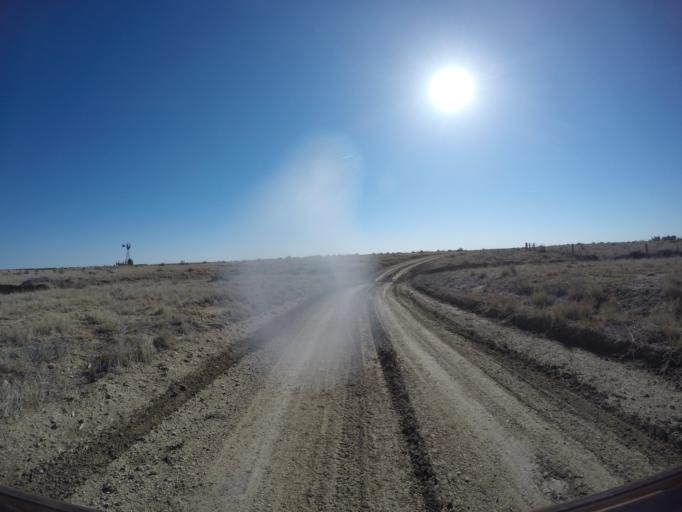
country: US
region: Colorado
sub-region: Otero County
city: La Junta
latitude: 37.6880
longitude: -103.6205
